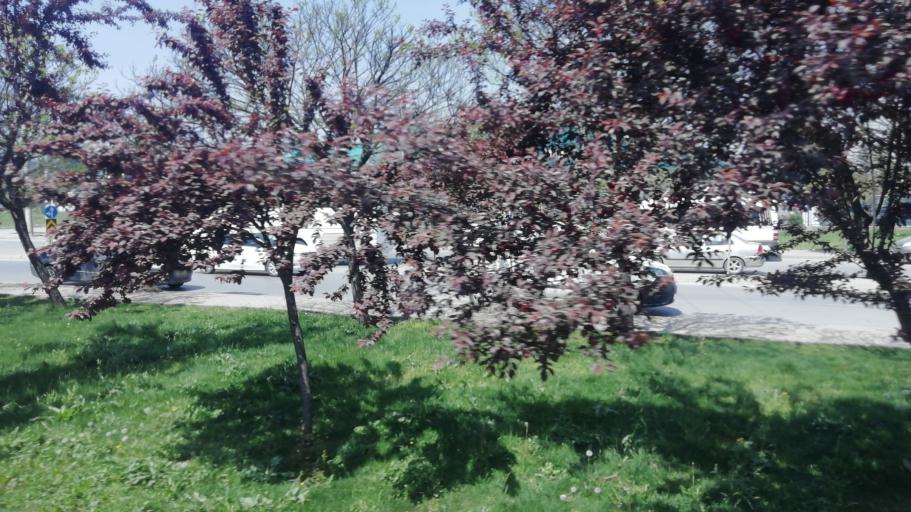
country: TR
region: Kocaeli
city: Gebze
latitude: 40.7945
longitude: 29.4583
